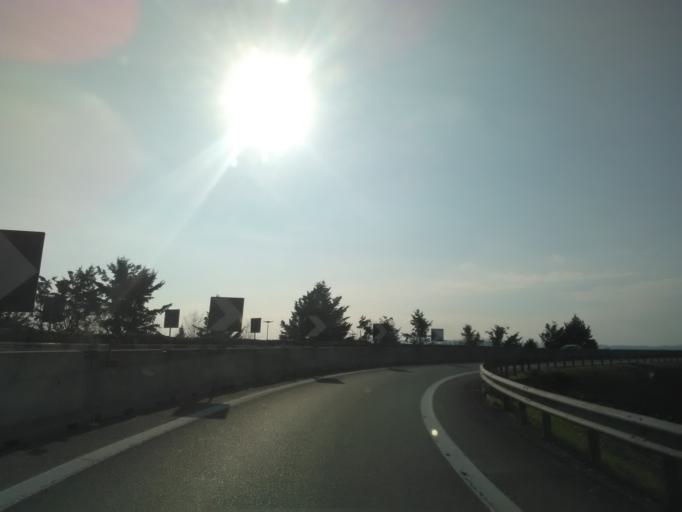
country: IT
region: Piedmont
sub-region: Provincia di Torino
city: Pavone Canavese
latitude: 45.4448
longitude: 7.8514
